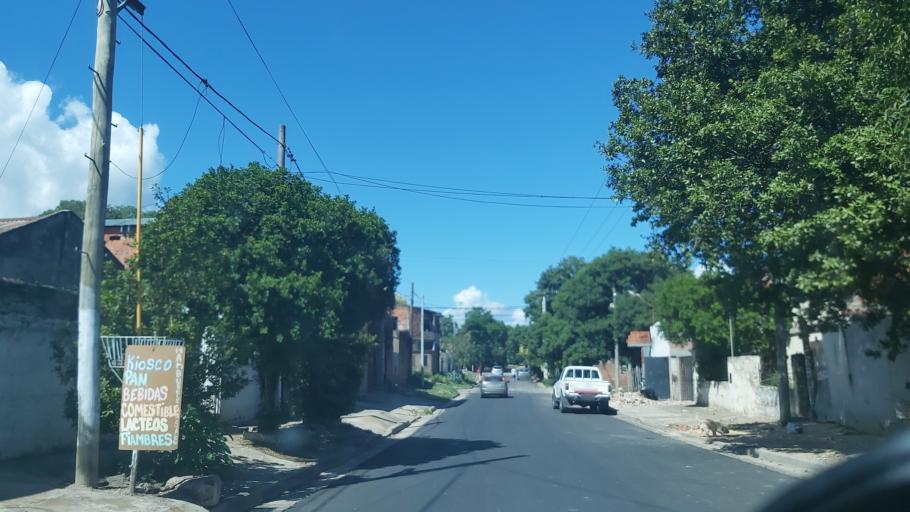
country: AR
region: Corrientes
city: Corrientes
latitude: -27.4823
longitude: -58.8479
